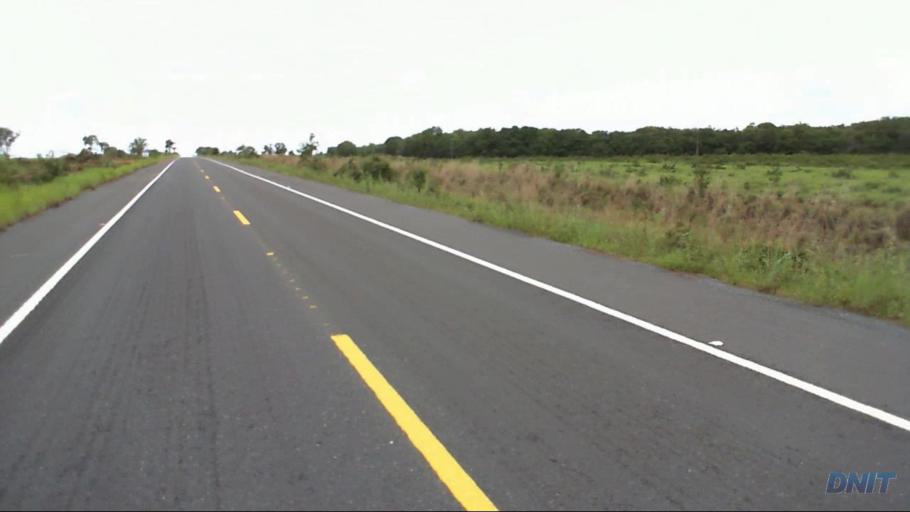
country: BR
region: Goias
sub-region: Sao Miguel Do Araguaia
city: Sao Miguel do Araguaia
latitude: -13.2894
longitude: -50.4359
